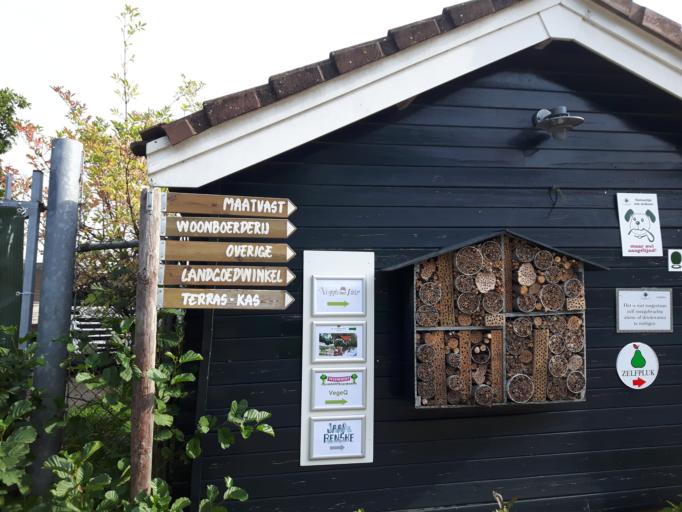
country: NL
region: South Holland
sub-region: Gemeente Lisse
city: Lisse
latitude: 52.2546
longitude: 4.5897
